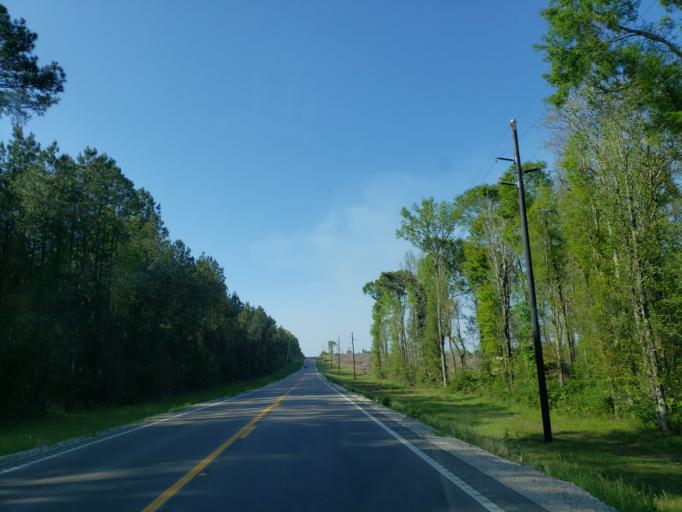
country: US
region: Mississippi
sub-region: Perry County
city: Richton
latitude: 31.2883
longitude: -88.9235
